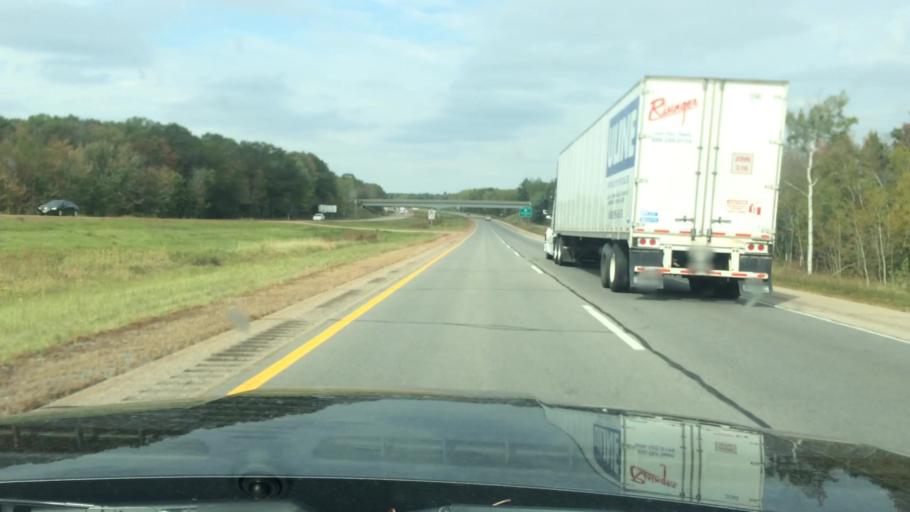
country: US
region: Wisconsin
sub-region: Marathon County
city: Mosinee
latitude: 44.7106
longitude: -89.6575
